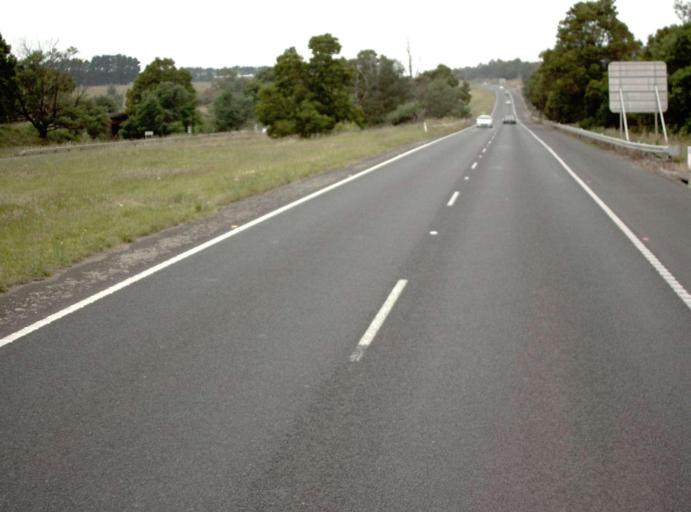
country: AU
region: Victoria
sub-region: Baw Baw
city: Warragul
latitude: -38.1802
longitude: 145.9847
